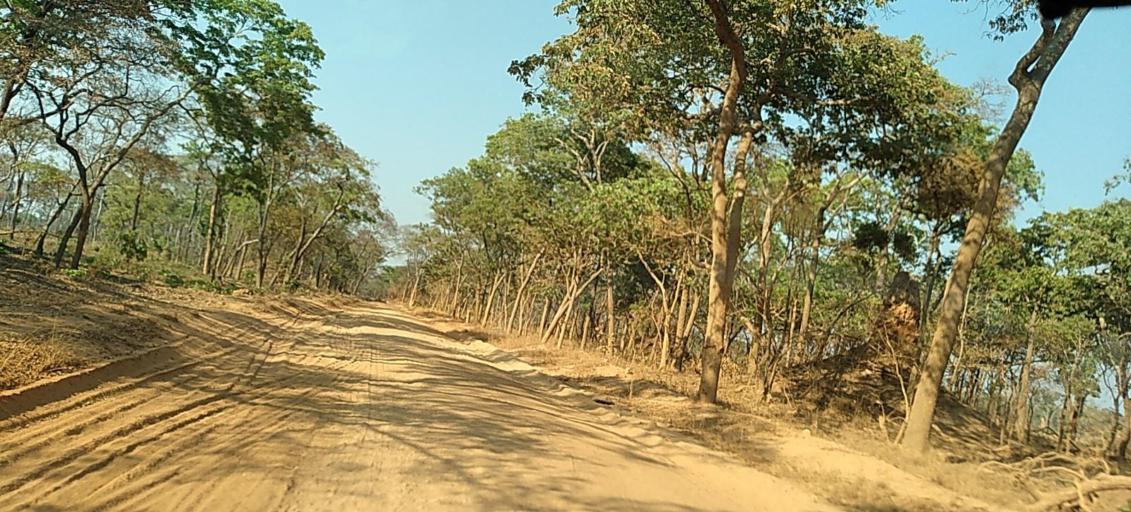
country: ZM
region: North-Western
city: Kasempa
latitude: -13.5908
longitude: 25.9840
